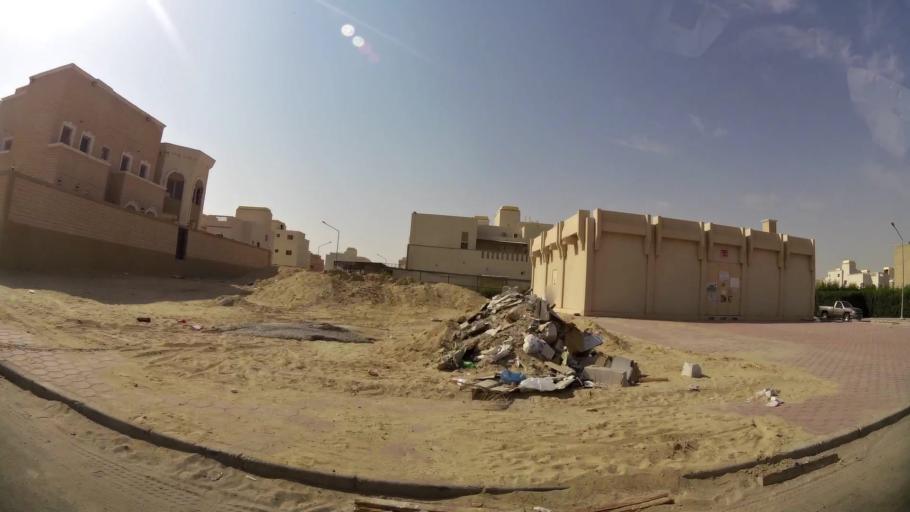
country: KW
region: Al Ahmadi
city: Al Wafrah
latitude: 28.7929
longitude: 48.0743
